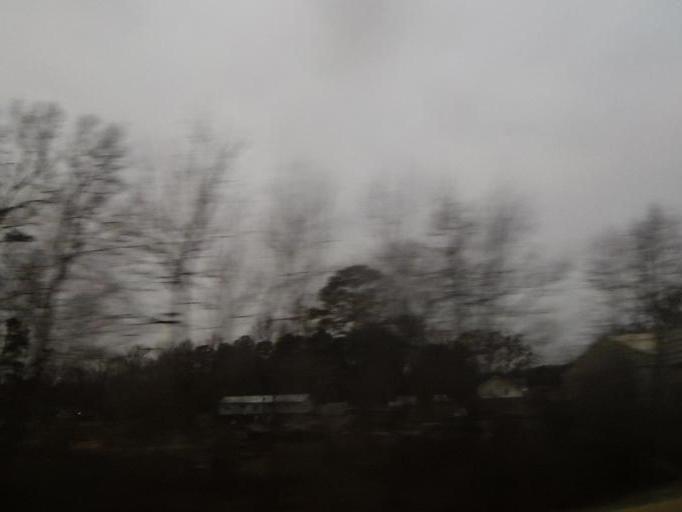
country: US
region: Alabama
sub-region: Cullman County
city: Cullman
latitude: 34.1577
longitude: -86.8728
